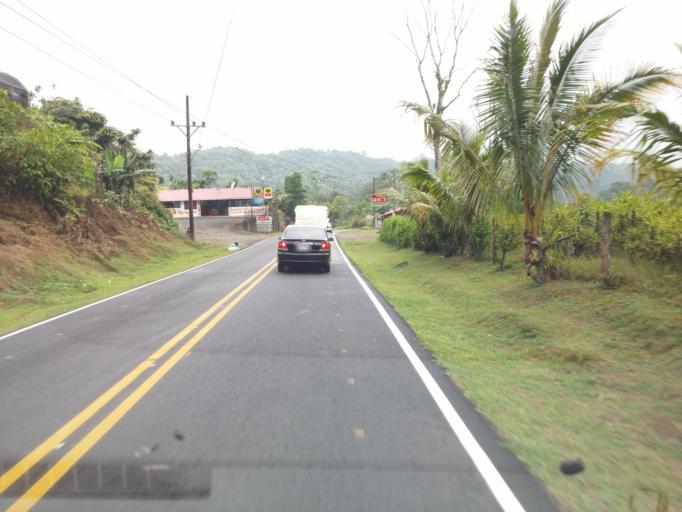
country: CR
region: Alajuela
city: San Ramon
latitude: 10.2129
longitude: -84.5432
